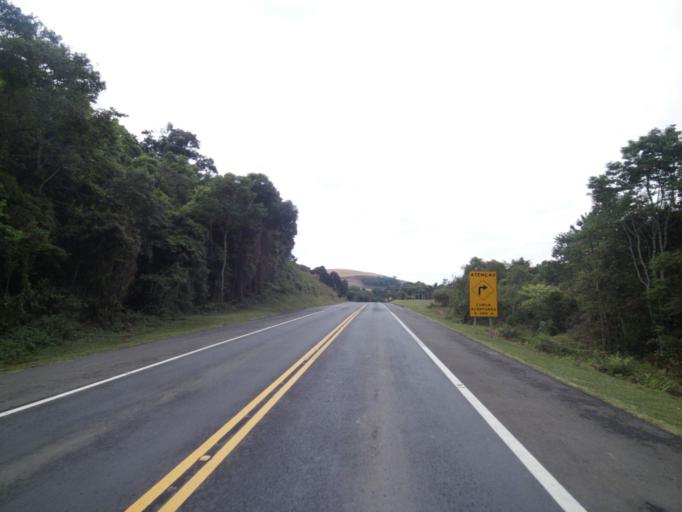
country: BR
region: Parana
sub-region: Irati
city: Irati
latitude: -25.4512
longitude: -50.6429
